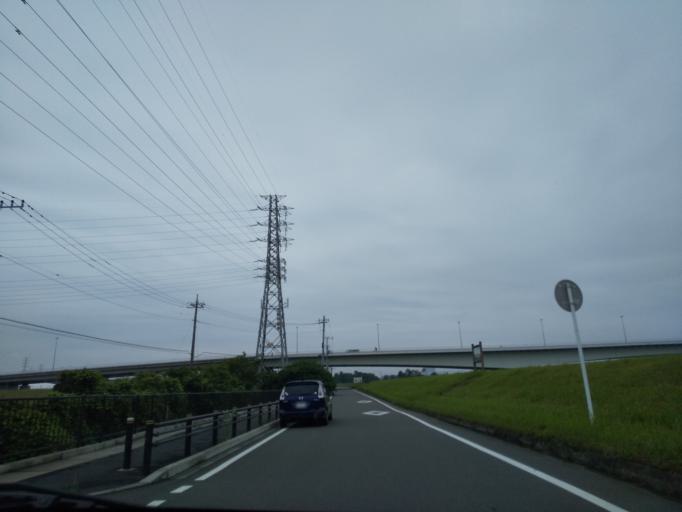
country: JP
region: Tokyo
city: Hino
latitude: 35.6714
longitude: 139.4257
